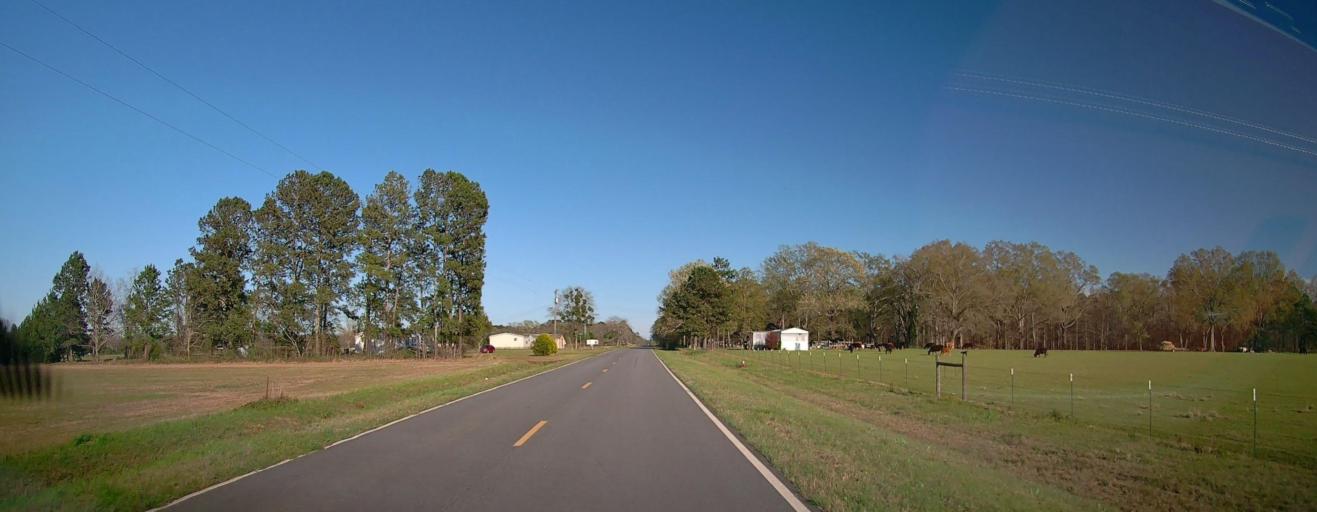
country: US
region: Georgia
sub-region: Pulaski County
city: Hawkinsville
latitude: 32.3478
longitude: -83.5935
